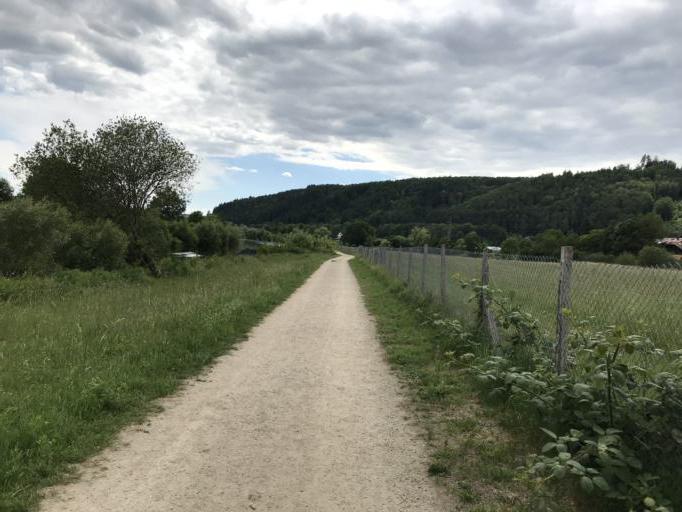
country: DE
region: Baden-Wuerttemberg
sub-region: Freiburg Region
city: Hausen
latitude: 47.6713
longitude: 7.8378
